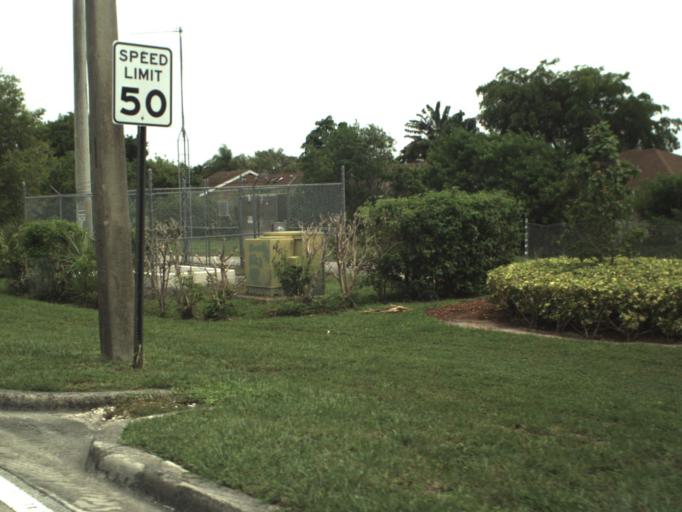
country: US
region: Florida
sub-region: Palm Beach County
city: Boca Pointe
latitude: 26.3502
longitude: -80.1683
